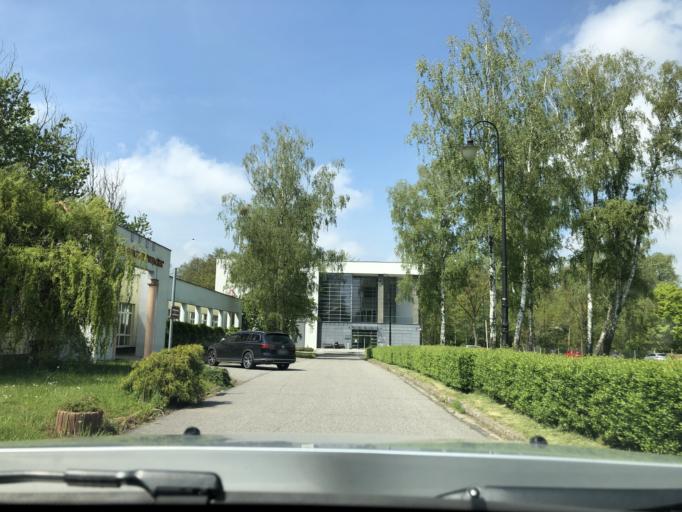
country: PL
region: Greater Poland Voivodeship
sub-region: Kalisz
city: Kalisz
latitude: 51.7724
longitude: 18.0345
